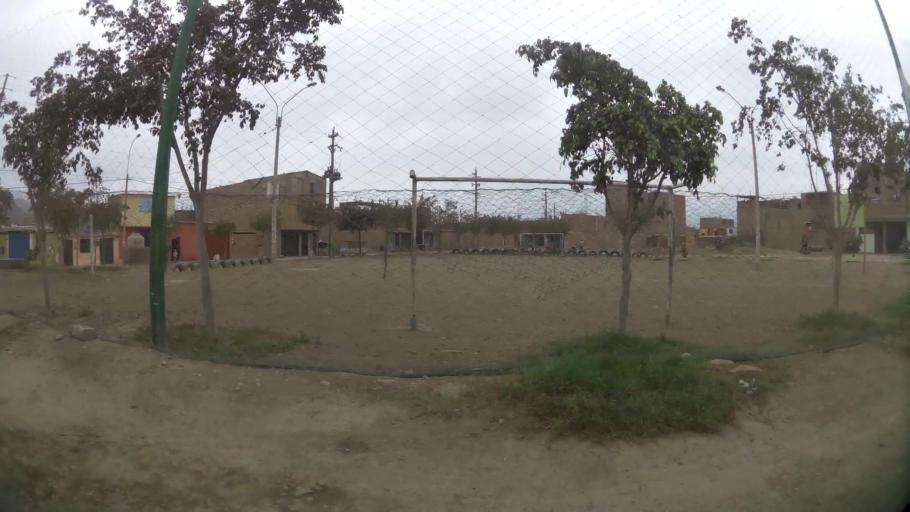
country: PE
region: Lima
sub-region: Lima
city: Independencia
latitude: -11.9558
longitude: -77.0980
